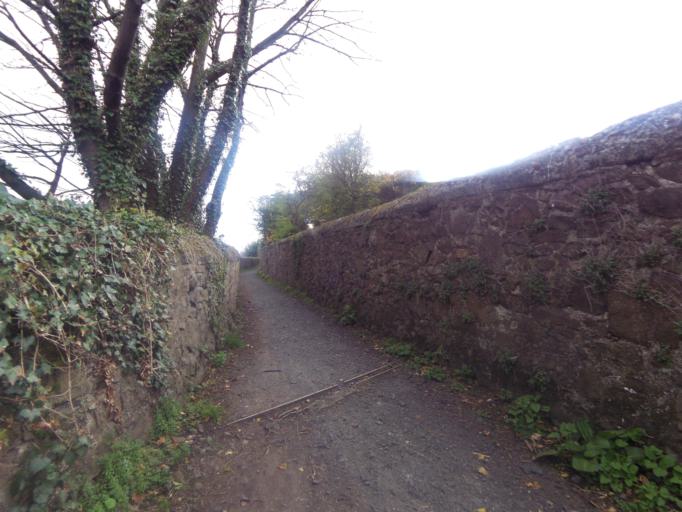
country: GB
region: Scotland
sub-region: Fife
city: Burntisland
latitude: 56.0611
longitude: -3.2518
